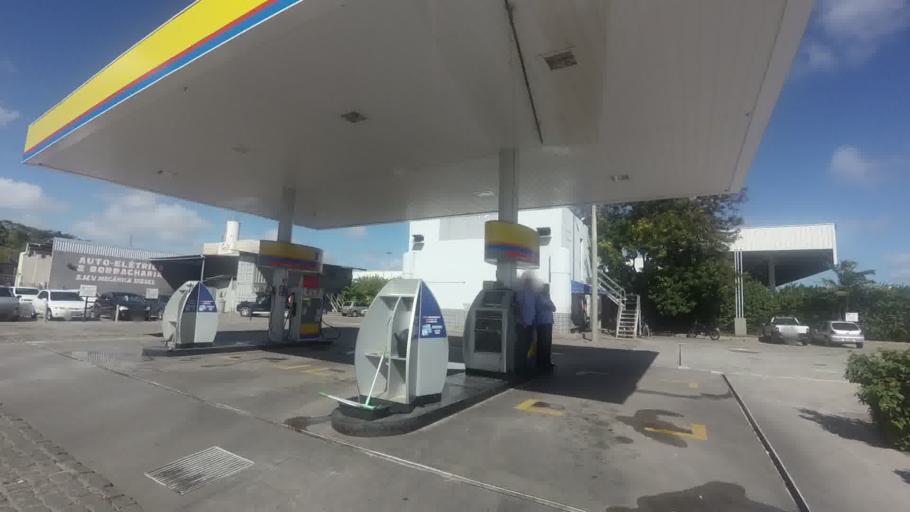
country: BR
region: Espirito Santo
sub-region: Serra
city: Serra
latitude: -20.2184
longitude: -40.2910
